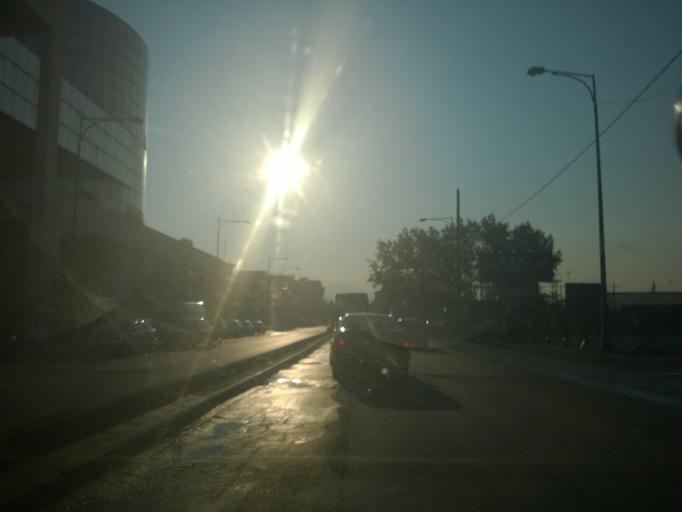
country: GR
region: Central Macedonia
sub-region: Nomos Thessalonikis
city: Ampelokipoi
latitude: 40.6431
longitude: 22.9115
